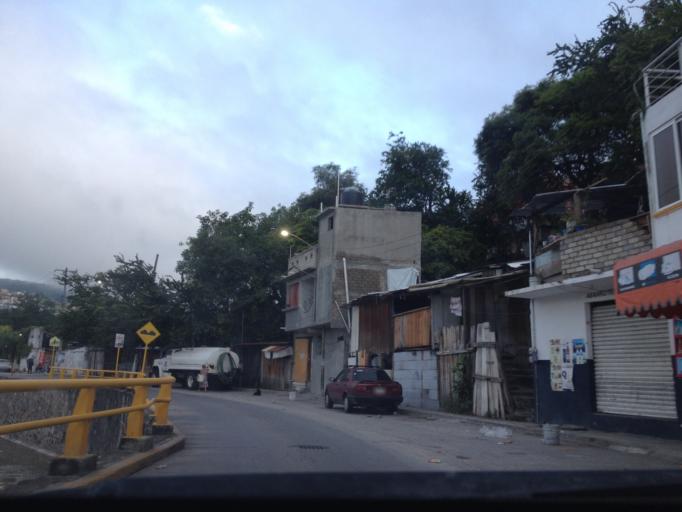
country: MX
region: Guerrero
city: Chilpancingo de los Bravos
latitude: 17.5490
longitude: -99.5022
